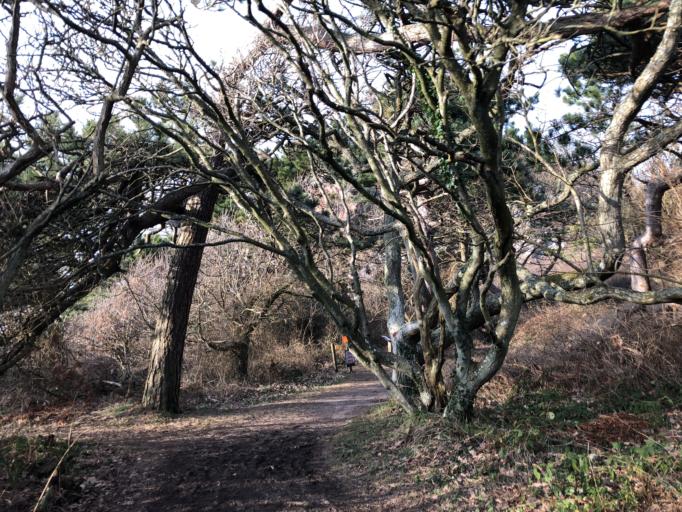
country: SE
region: Skane
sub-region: Hoganas Kommun
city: Hoganas
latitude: 56.2995
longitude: 12.4526
